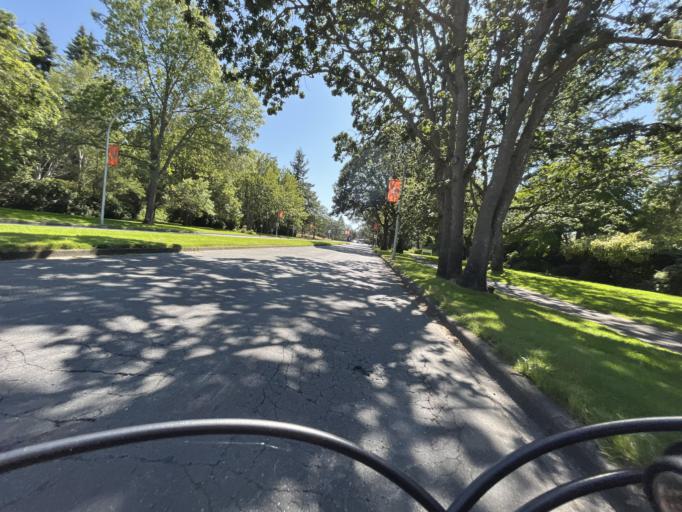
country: CA
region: British Columbia
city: Oak Bay
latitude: 48.4603
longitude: -123.3146
